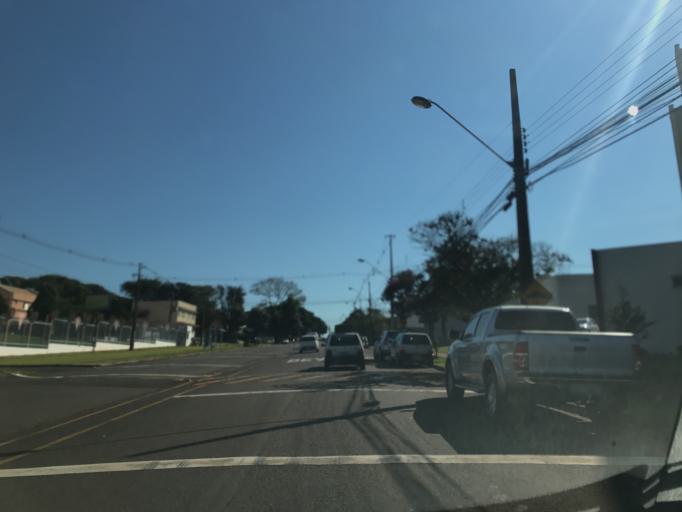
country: BR
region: Parana
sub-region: Maringa
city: Maringa
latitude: -23.4533
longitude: -51.9534
